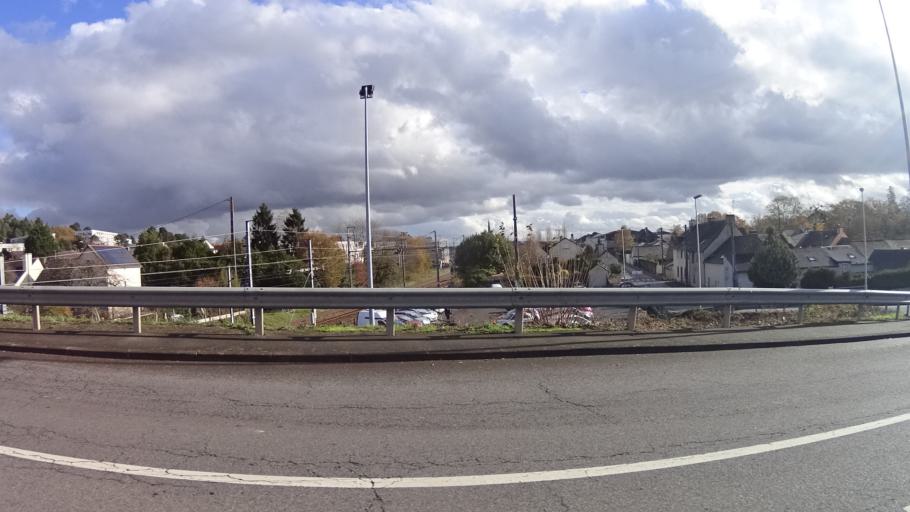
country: FR
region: Brittany
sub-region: Departement d'Ille-et-Vilaine
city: Redon
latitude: 47.6534
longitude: -2.0979
